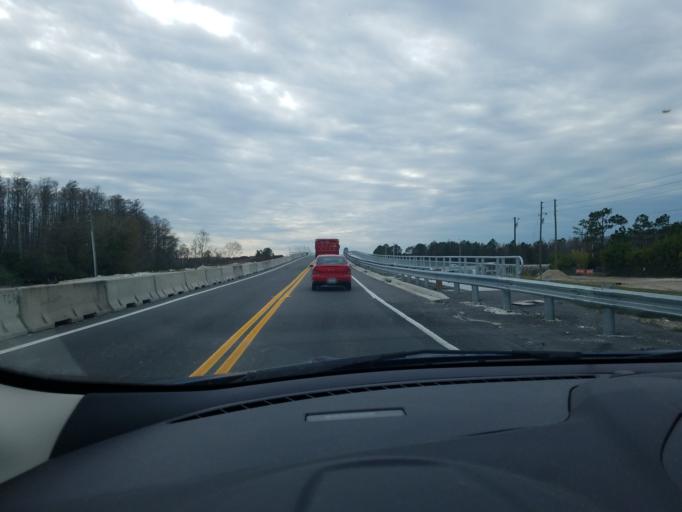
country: US
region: Florida
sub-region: Orange County
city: Meadow Woods
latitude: 28.3613
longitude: -81.3862
